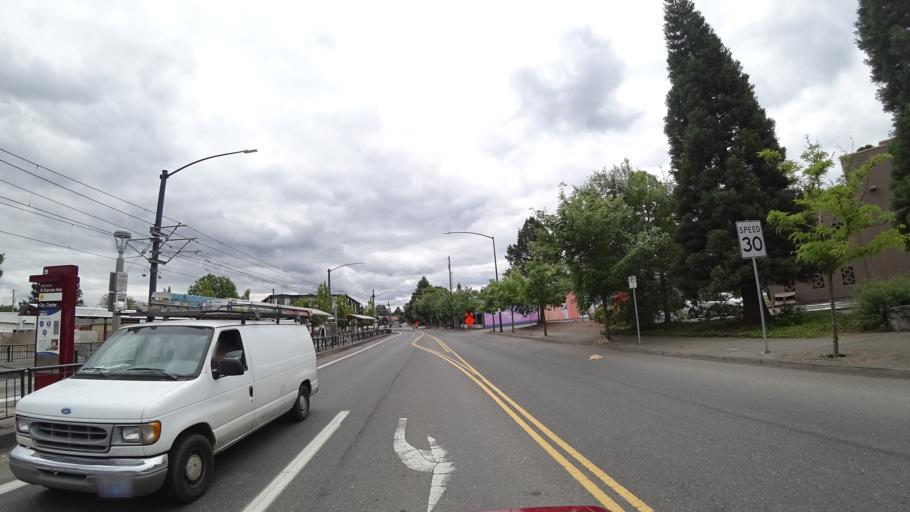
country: US
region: Washington
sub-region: Clark County
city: Vancouver
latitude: 45.5839
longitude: -122.6864
